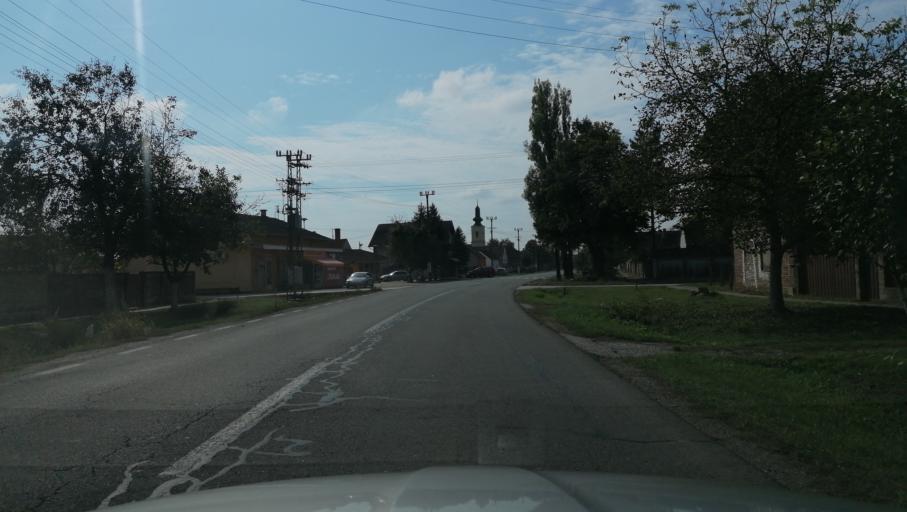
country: RS
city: Bosut
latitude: 44.9343
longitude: 19.3663
